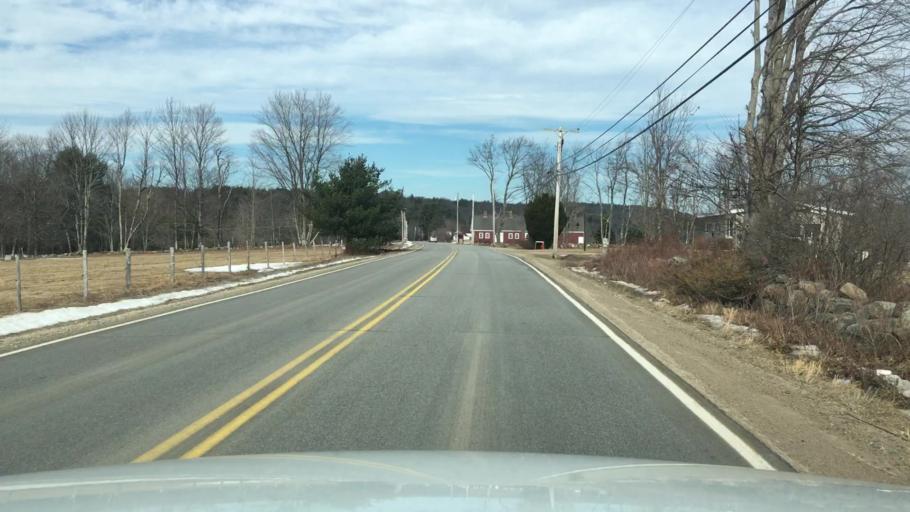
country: US
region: Maine
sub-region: York County
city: Springvale
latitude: 43.4943
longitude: -70.8098
